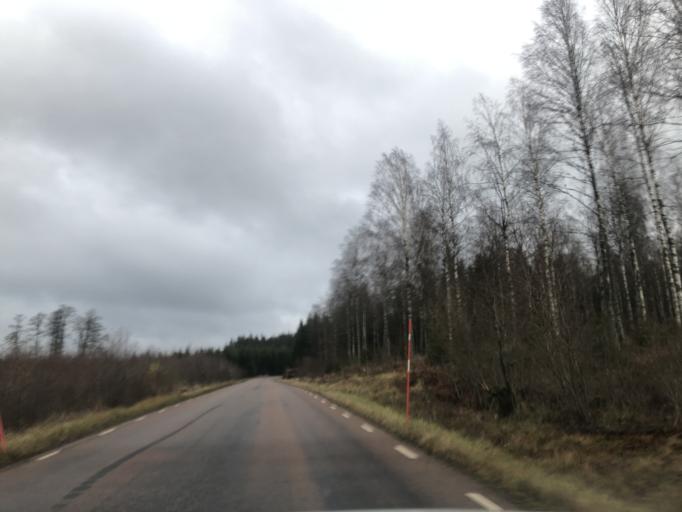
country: SE
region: Vaestra Goetaland
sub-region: Ulricehamns Kommun
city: Ulricehamn
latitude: 57.8319
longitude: 13.4931
